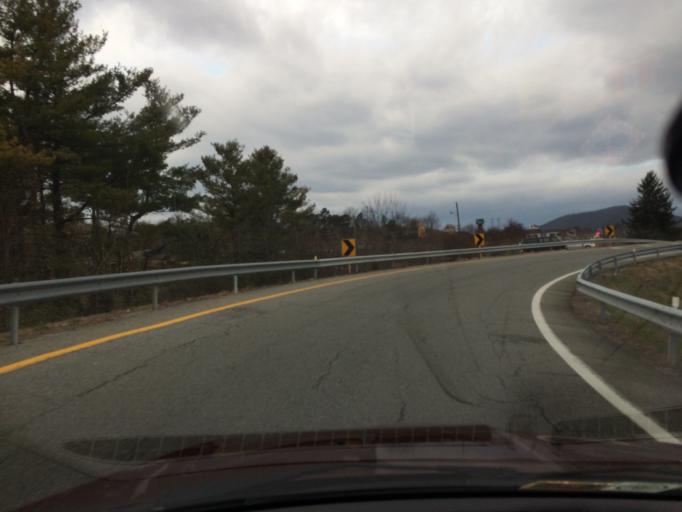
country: US
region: Virginia
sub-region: Roanoke County
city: Hollins
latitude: 37.3256
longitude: -79.9898
